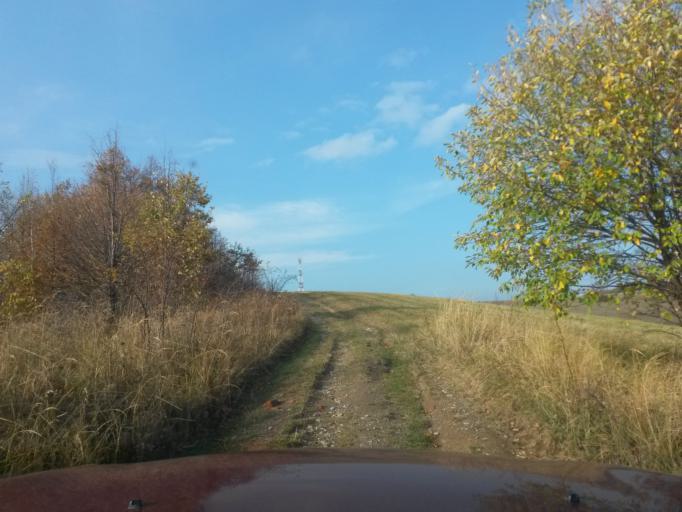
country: SK
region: Kosicky
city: Kosice
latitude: 48.7627
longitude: 21.2115
